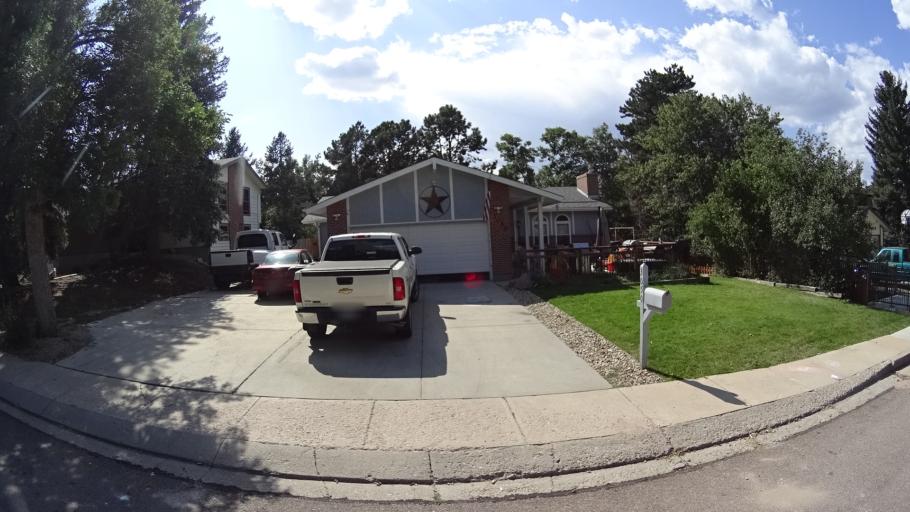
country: US
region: Colorado
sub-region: El Paso County
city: Cimarron Hills
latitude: 38.8751
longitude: -104.7420
